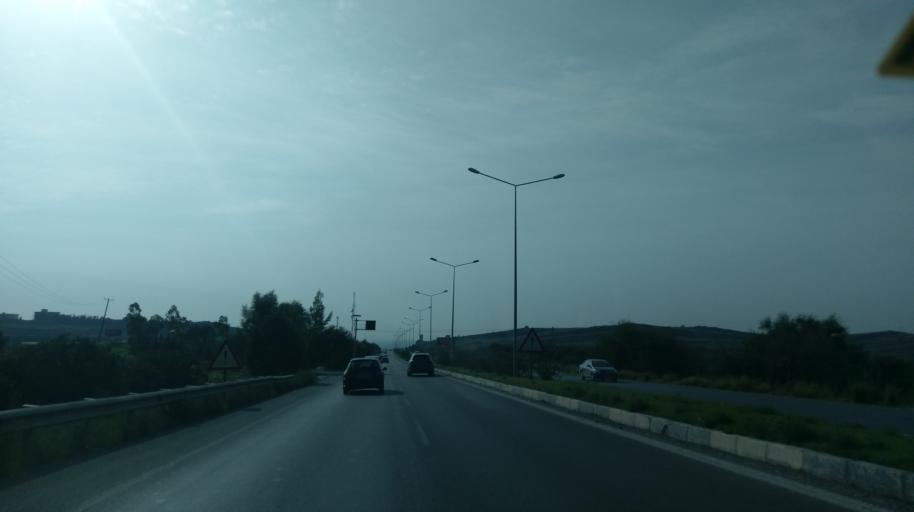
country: CY
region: Lefkosia
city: Nicosia
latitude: 35.2379
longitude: 33.3112
